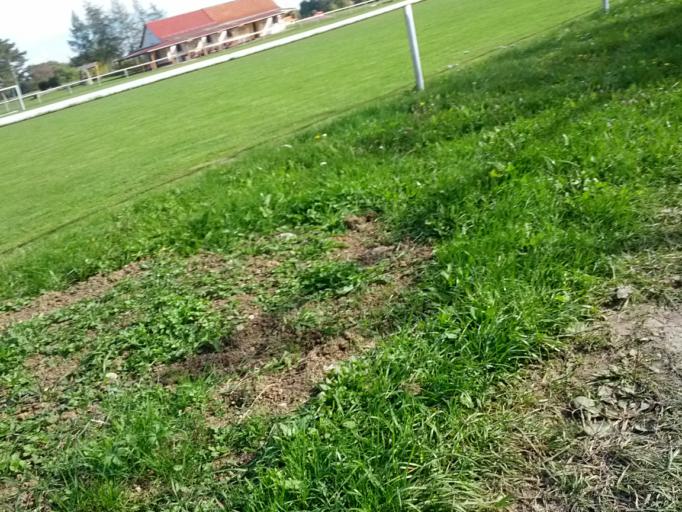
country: DE
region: Thuringia
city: Krauthausen
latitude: 51.0386
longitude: 10.2906
